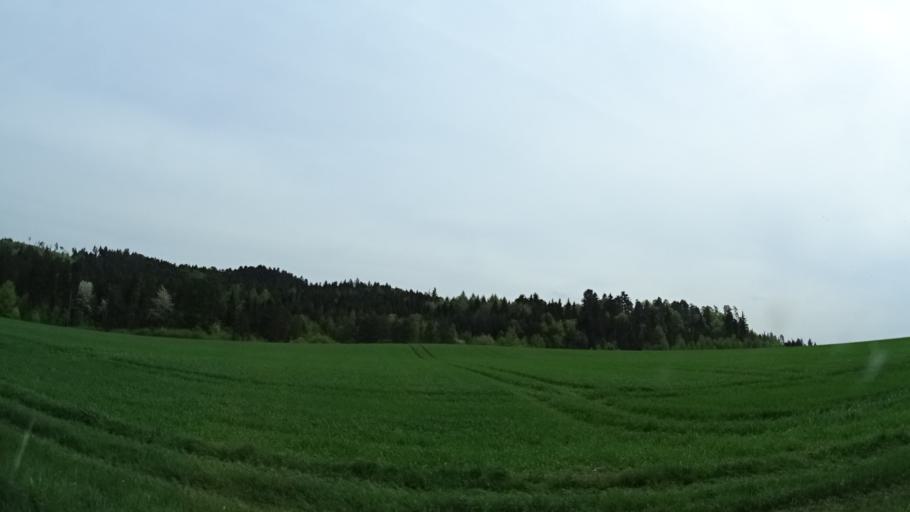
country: DE
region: Baden-Wuerttemberg
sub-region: Freiburg Region
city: Deisslingen
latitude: 48.0944
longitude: 8.5931
